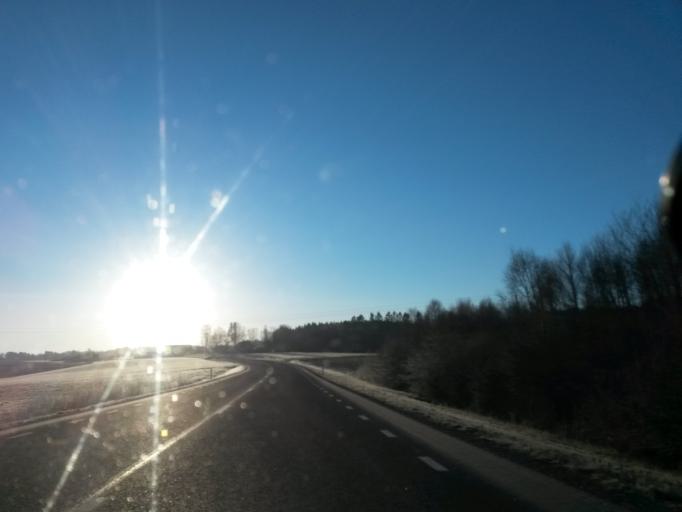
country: SE
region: Vaestra Goetaland
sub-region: Vargarda Kommun
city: Vargarda
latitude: 58.0489
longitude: 12.8248
